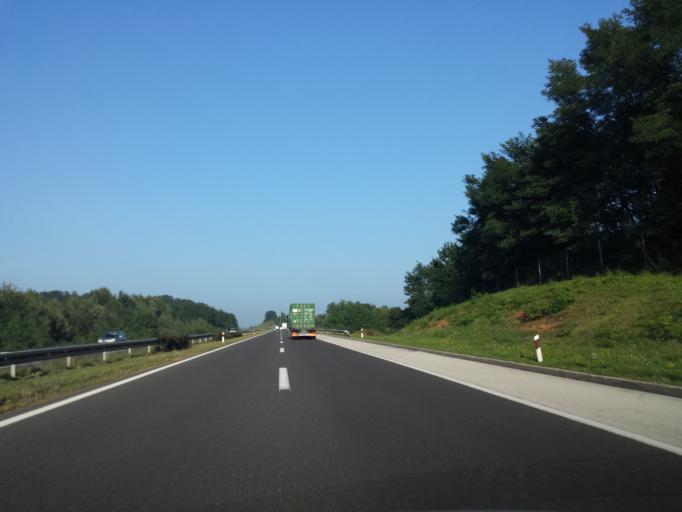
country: HR
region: Karlovacka
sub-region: Grad Karlovac
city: Karlovac
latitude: 45.4642
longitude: 15.3963
